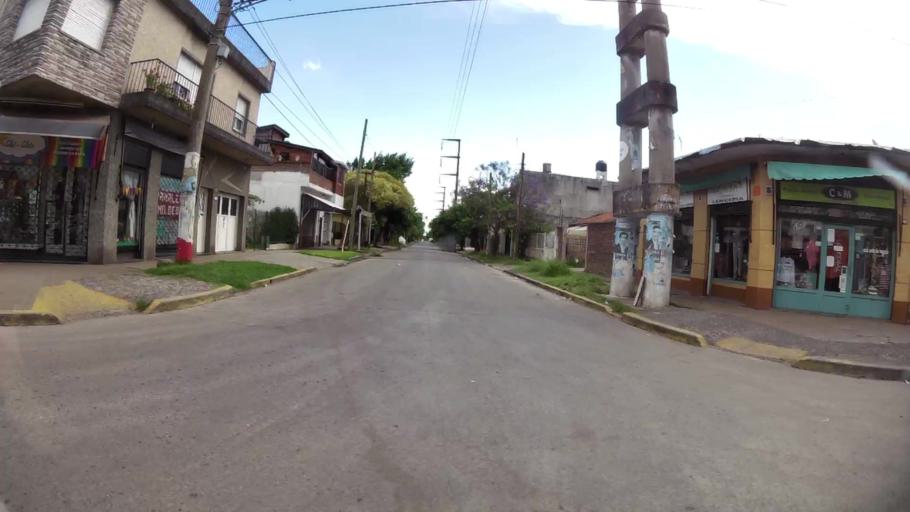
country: AR
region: Buenos Aires
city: Ituzaingo
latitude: -34.6394
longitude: -58.6892
